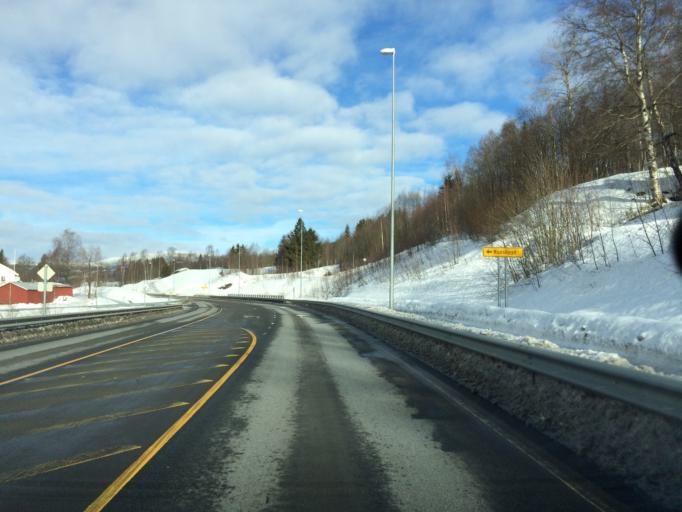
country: NO
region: Oppland
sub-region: Gausdal
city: Segalstad bru
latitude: 61.1895
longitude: 10.3178
